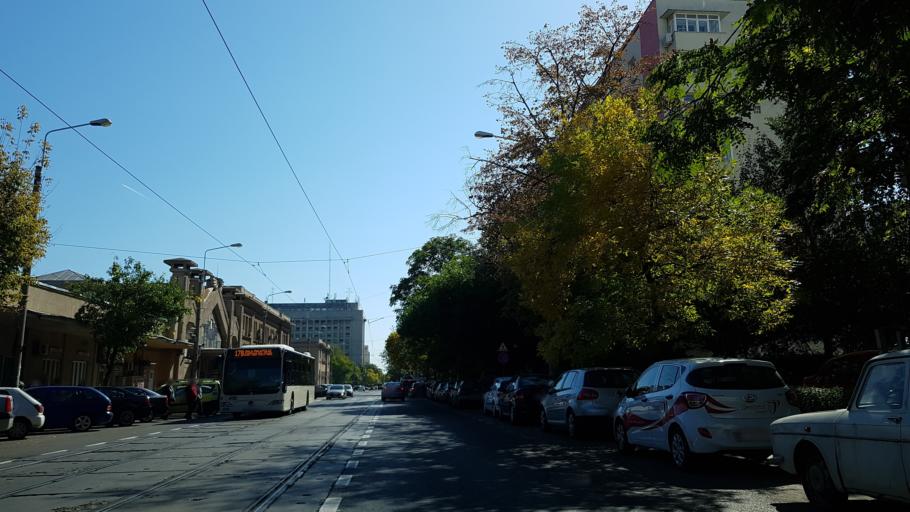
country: RO
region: Bucuresti
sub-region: Municipiul Bucuresti
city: Bucuresti
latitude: 44.4467
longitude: 26.0725
